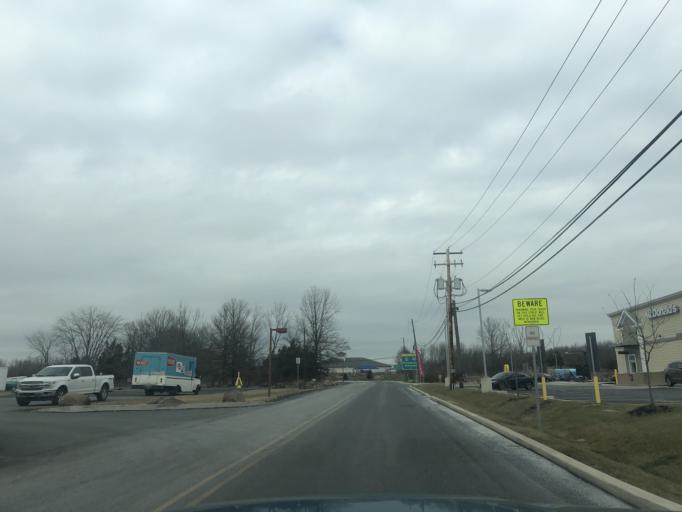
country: US
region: Pennsylvania
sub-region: Bucks County
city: Spinnerstown
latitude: 40.4352
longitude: -75.4186
